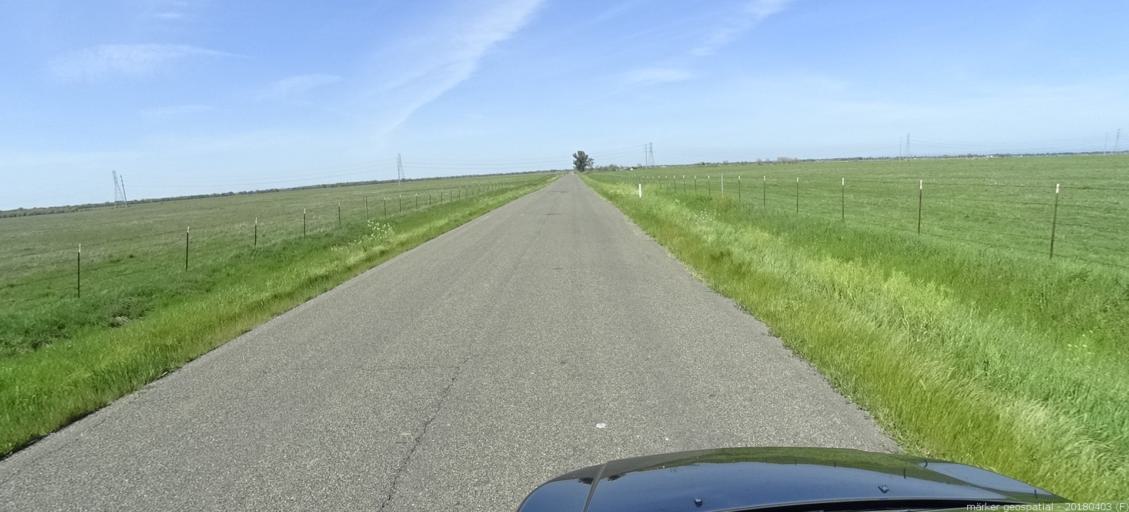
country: US
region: California
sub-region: Sacramento County
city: Herald
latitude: 38.3442
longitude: -121.2976
